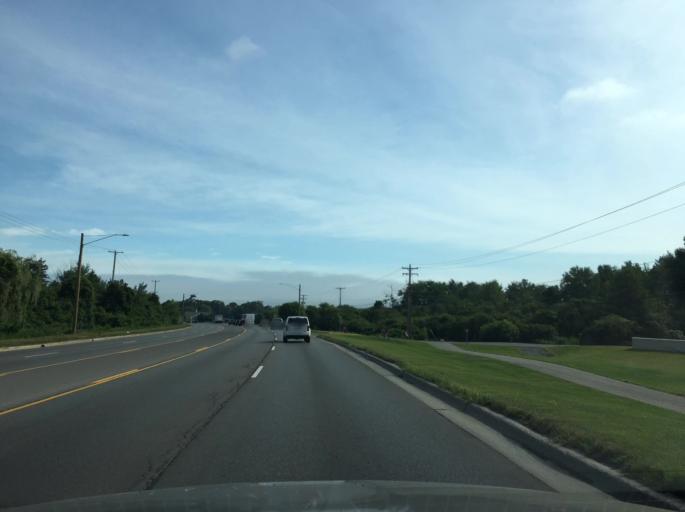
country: US
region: Michigan
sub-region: Grand Traverse County
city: Traverse City
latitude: 44.7477
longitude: -85.6365
